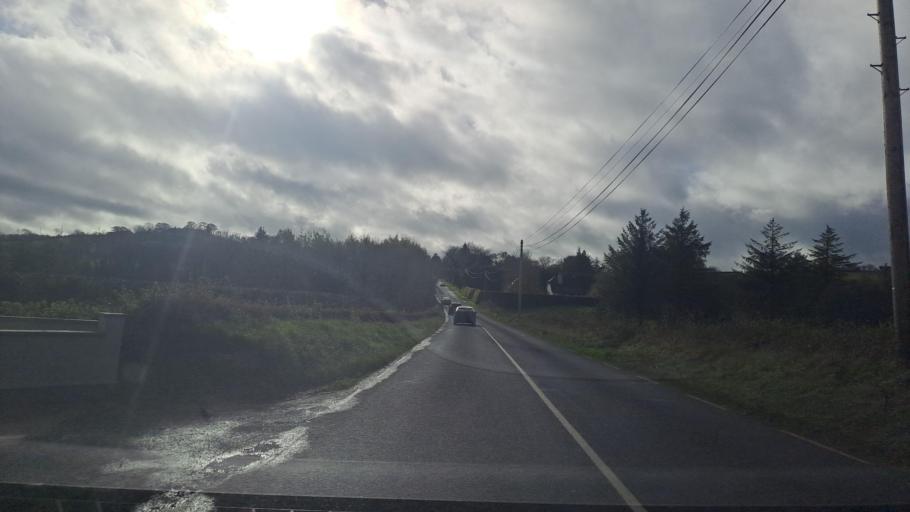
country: IE
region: Ulster
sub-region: County Monaghan
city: Monaghan
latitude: 54.1968
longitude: -6.9893
